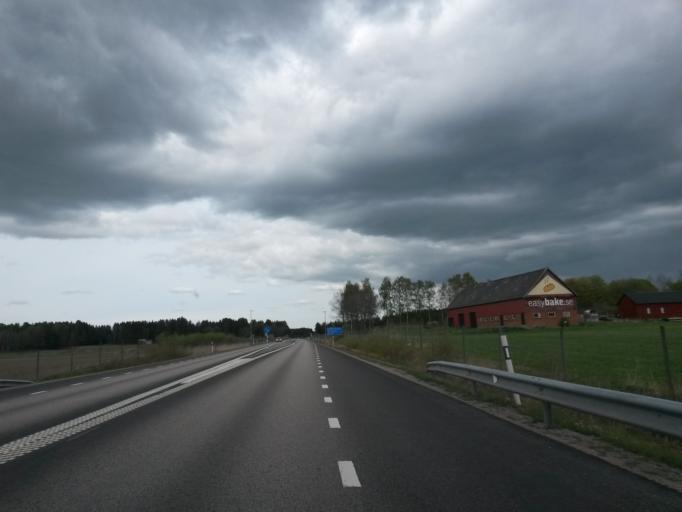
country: SE
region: Vaestra Goetaland
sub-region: Vara Kommun
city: Vara
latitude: 58.1689
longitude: 12.8878
